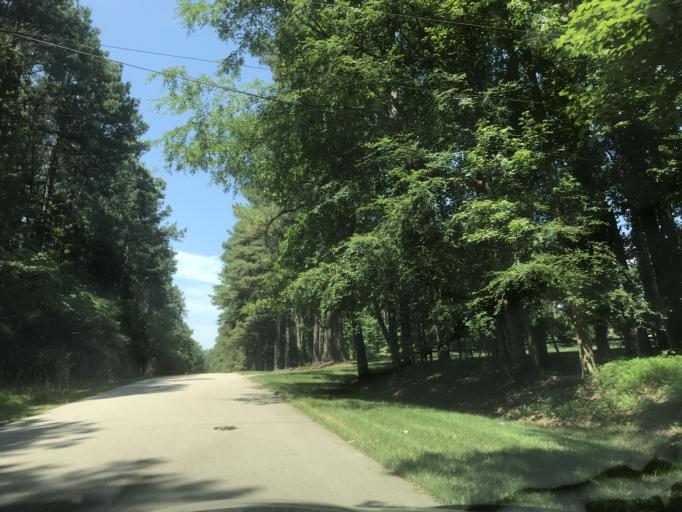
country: US
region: North Carolina
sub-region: Wake County
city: Wake Forest
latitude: 35.9085
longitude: -78.6127
